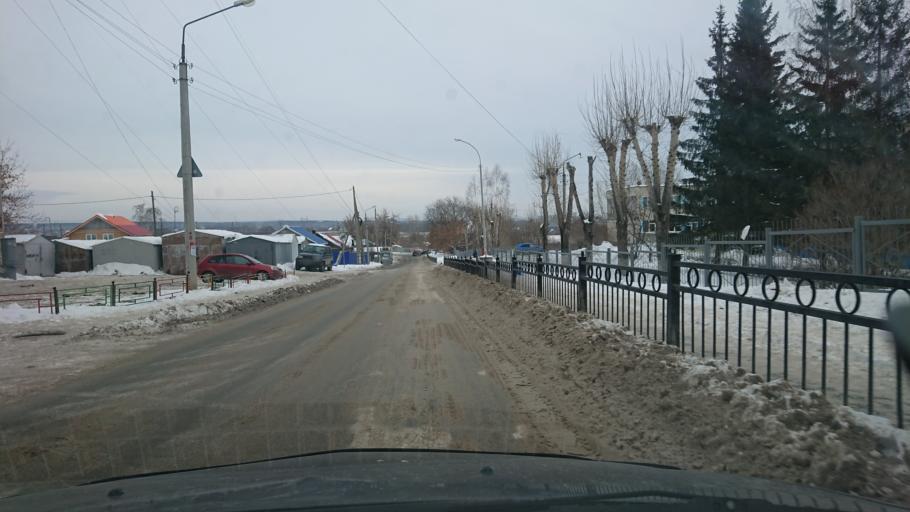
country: RU
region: Sverdlovsk
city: Istok
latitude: 56.7816
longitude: 60.7399
